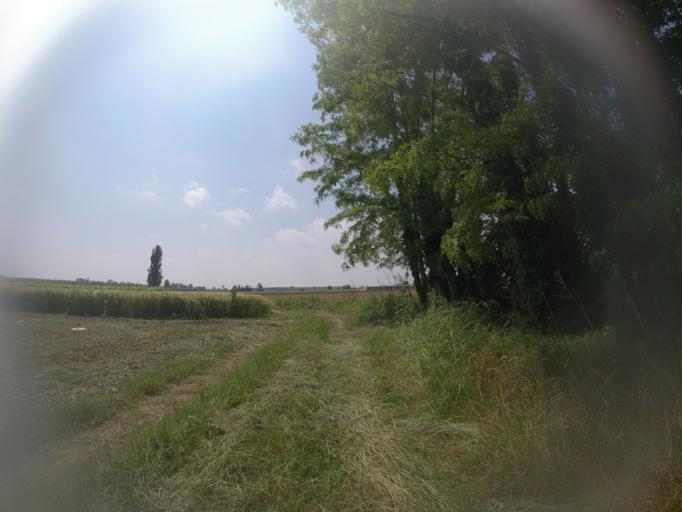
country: IT
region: Friuli Venezia Giulia
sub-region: Provincia di Udine
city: Bertiolo
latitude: 45.9353
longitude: 13.0431
